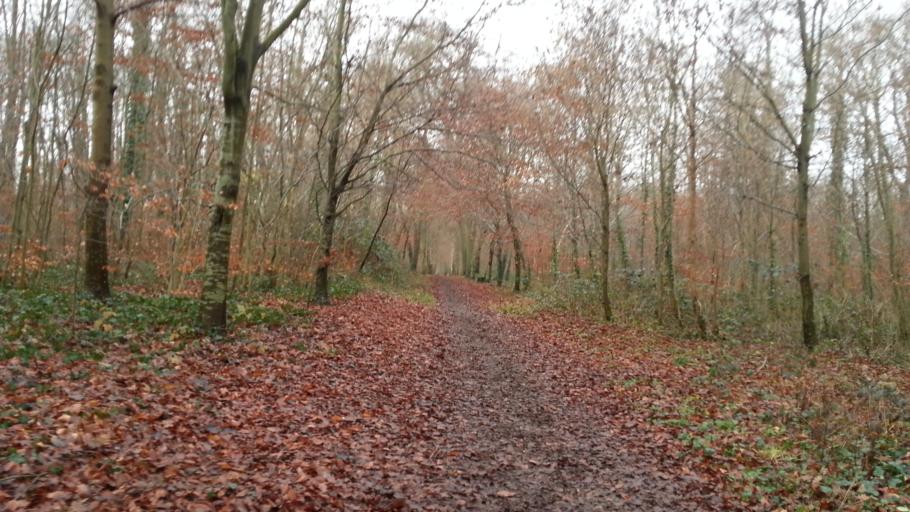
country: FR
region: Picardie
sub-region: Departement de l'Oise
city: Gouvieux
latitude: 49.1851
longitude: 2.4016
